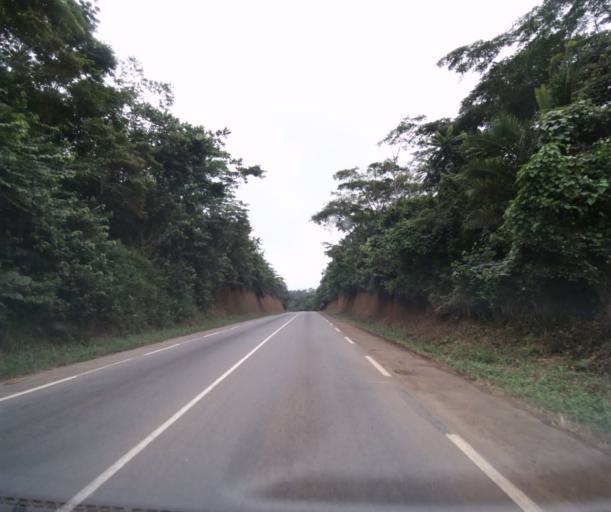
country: CM
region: Centre
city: Mbankomo
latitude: 3.7725
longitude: 11.1667
